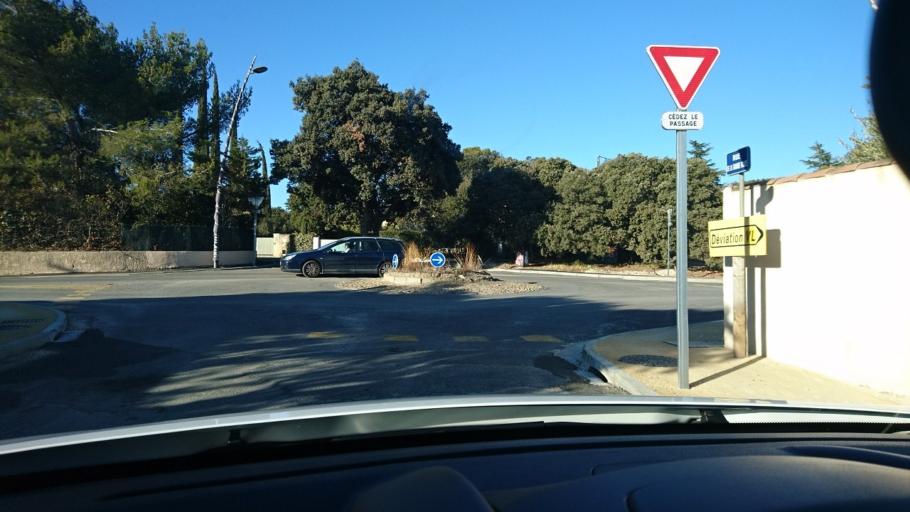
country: FR
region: Languedoc-Roussillon
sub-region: Departement du Gard
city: Les Angles
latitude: 43.9634
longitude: 4.7591
